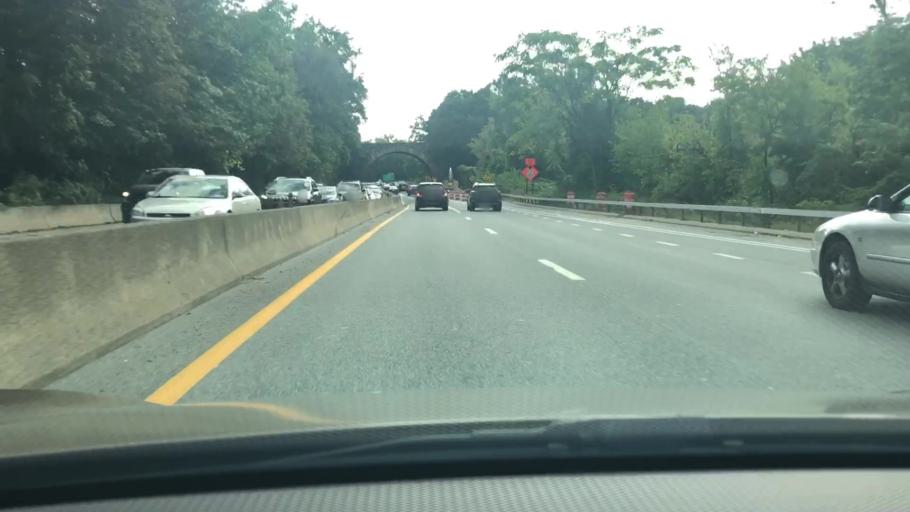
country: US
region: New York
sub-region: Westchester County
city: Pelham
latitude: 40.9132
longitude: -73.8130
